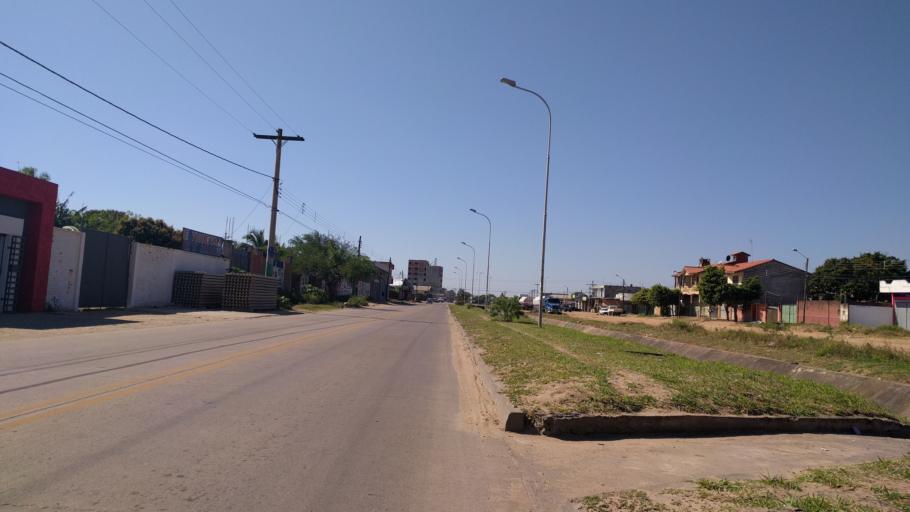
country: BO
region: Santa Cruz
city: Santa Cruz de la Sierra
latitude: -17.8440
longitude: -63.1836
